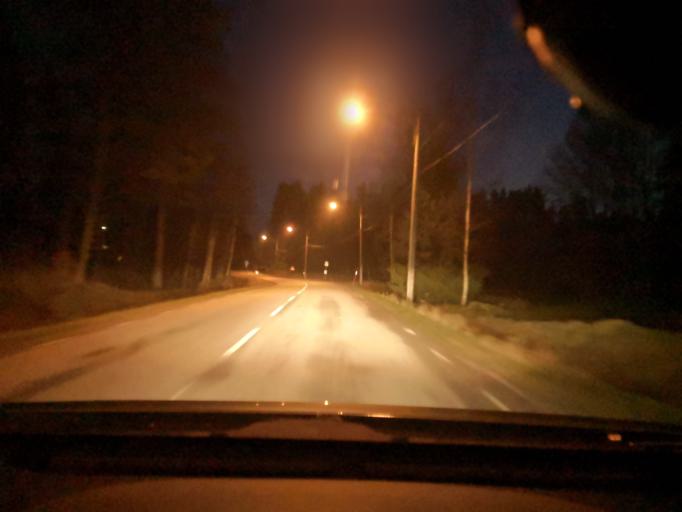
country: SE
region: OErebro
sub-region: Hallsbergs Kommun
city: Skollersta
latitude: 59.2171
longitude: 15.3438
